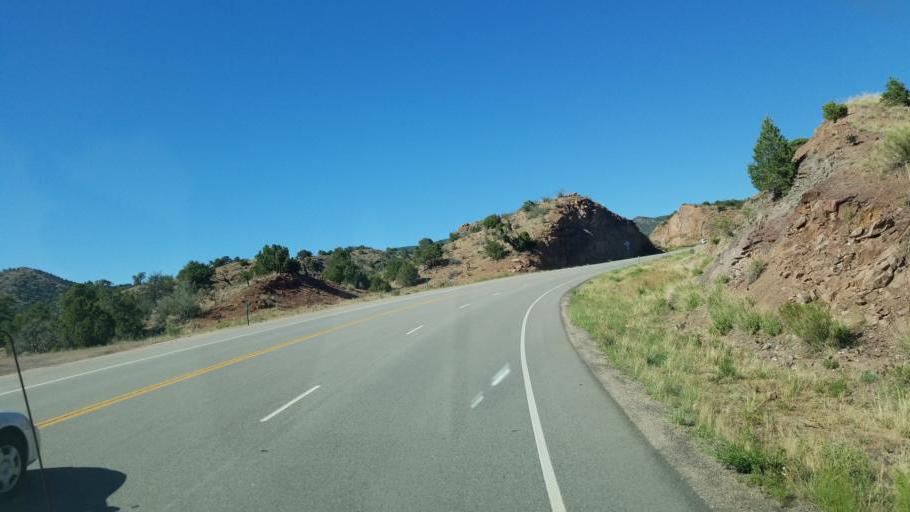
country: US
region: Colorado
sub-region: Fremont County
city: Canon City
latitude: 38.4938
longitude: -105.3634
